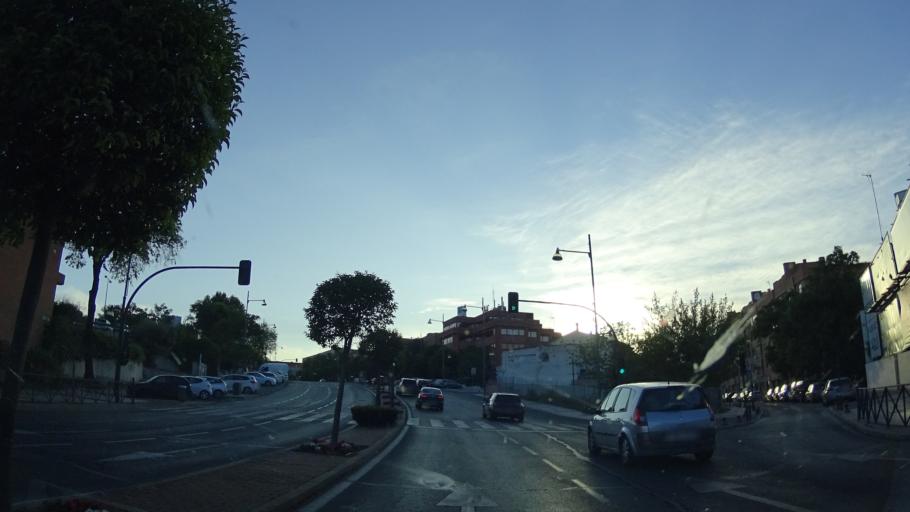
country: ES
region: Madrid
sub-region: Provincia de Madrid
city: Alcobendas
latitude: 40.5480
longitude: -3.6370
